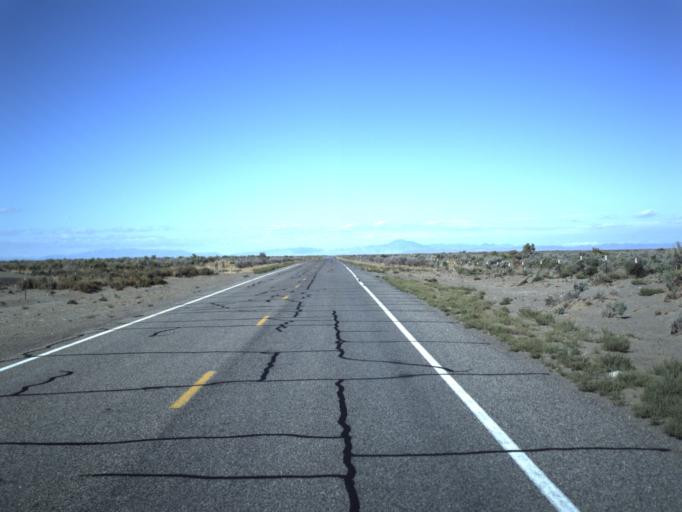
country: US
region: Utah
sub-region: Millard County
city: Delta
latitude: 39.3541
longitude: -112.4332
